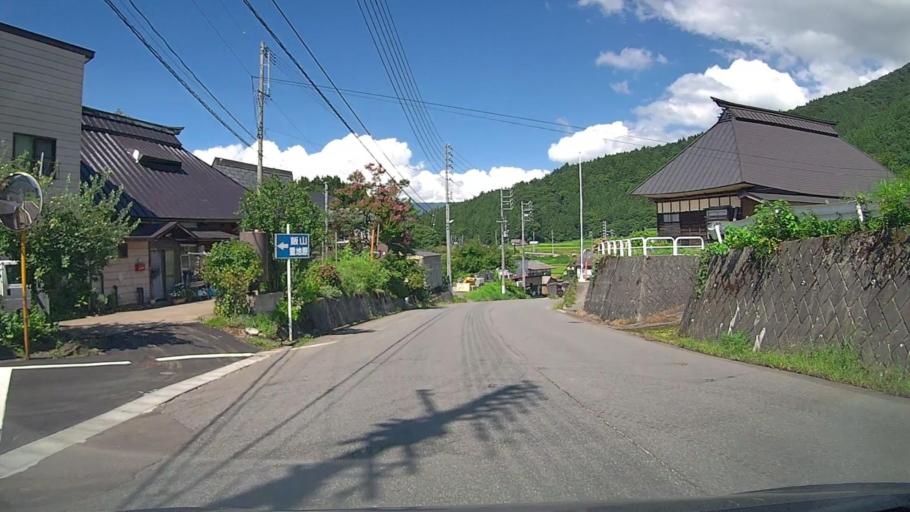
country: JP
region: Nagano
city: Iiyama
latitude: 36.9324
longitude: 138.4243
